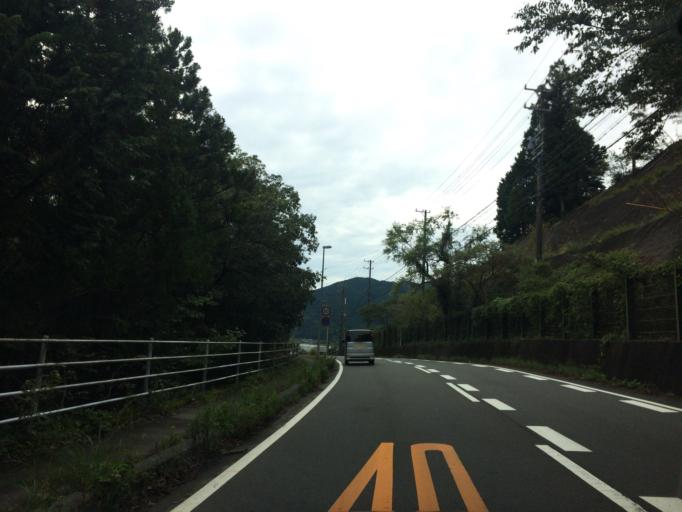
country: JP
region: Shizuoka
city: Kanaya
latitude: 35.0522
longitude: 138.0902
